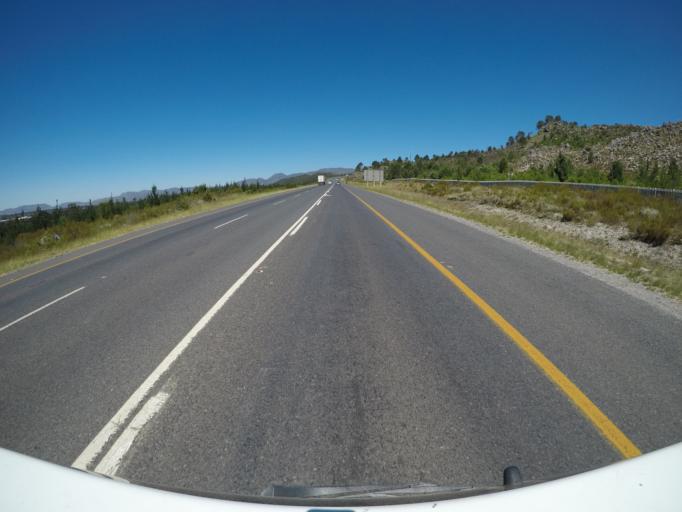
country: ZA
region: Western Cape
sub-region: Overberg District Municipality
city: Grabouw
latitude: -34.1641
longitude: 19.0059
